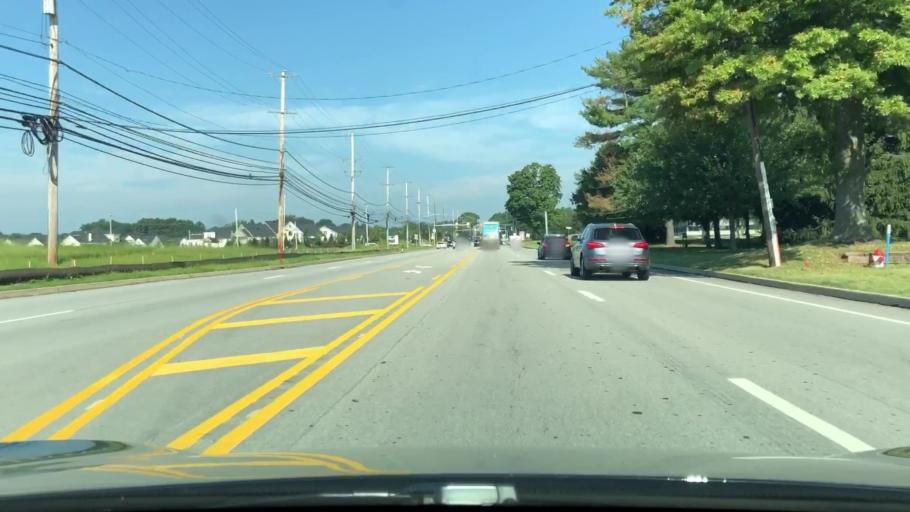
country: US
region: Pennsylvania
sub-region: Montgomery County
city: Horsham
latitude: 40.1595
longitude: -75.1473
